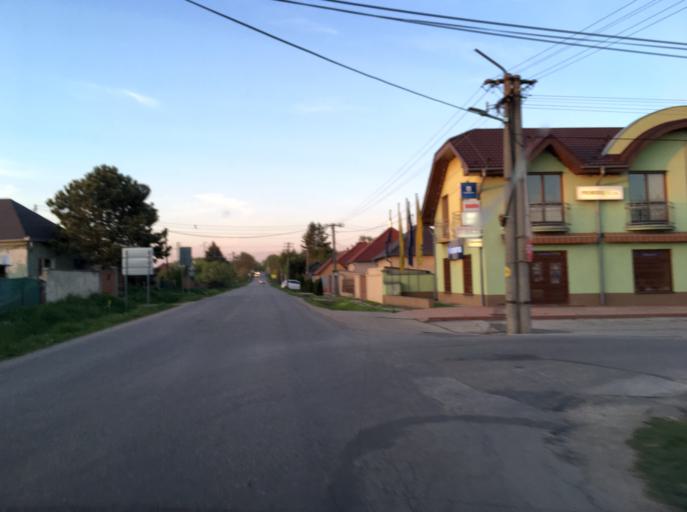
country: SK
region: Nitriansky
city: Kolarovo
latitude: 47.9103
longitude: 18.0068
